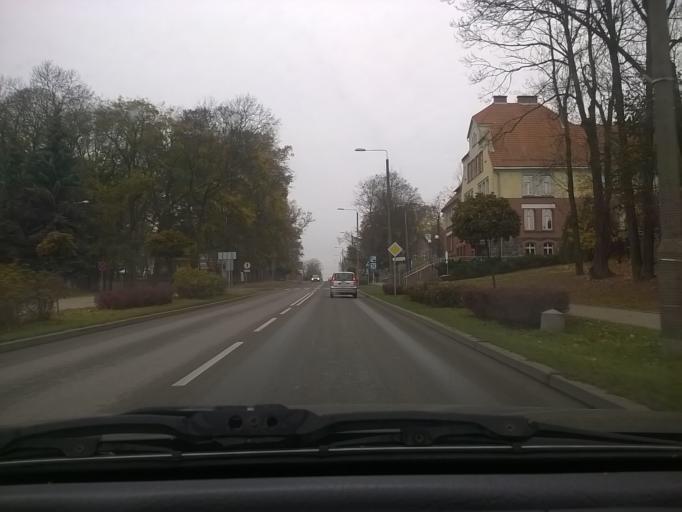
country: PL
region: Warmian-Masurian Voivodeship
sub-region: Powiat ketrzynski
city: Ketrzyn
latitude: 54.0825
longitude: 21.3572
